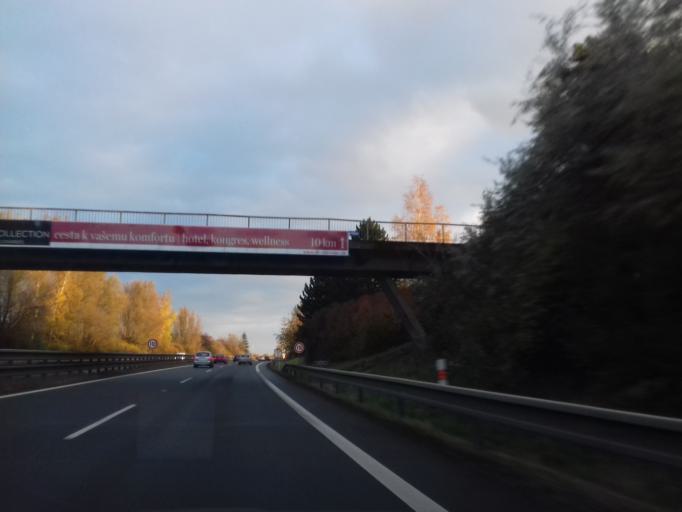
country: CZ
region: Olomoucky
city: Smrzice
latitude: 49.5013
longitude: 17.1415
